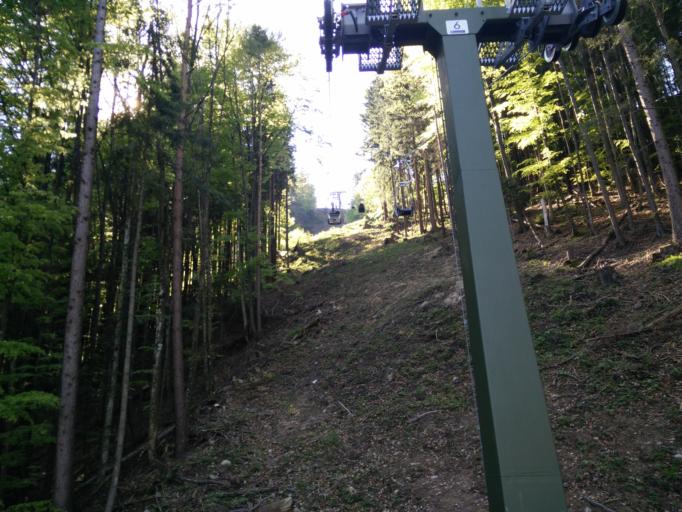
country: AT
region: Tyrol
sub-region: Politischer Bezirk Kufstein
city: Kufstein
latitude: 47.5879
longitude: 12.1903
